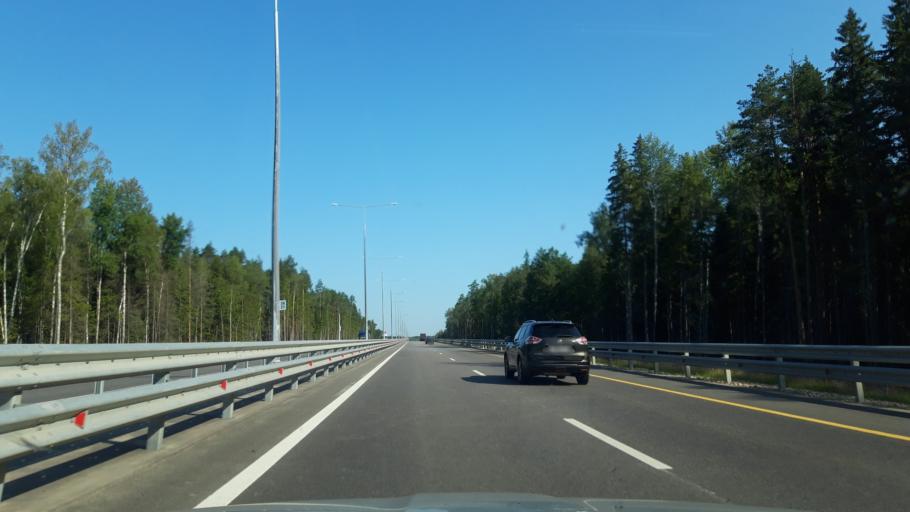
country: RU
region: Moskovskaya
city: Reshetnikovo
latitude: 56.4190
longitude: 36.5533
